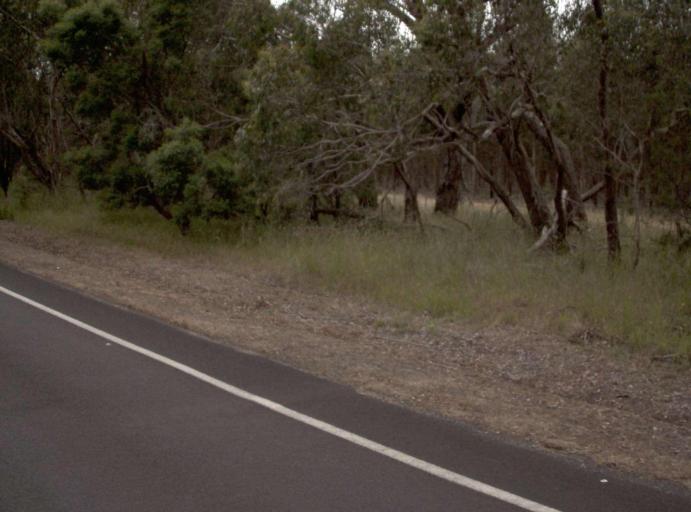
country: AU
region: Victoria
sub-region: Wellington
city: Sale
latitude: -38.4207
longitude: 146.9579
